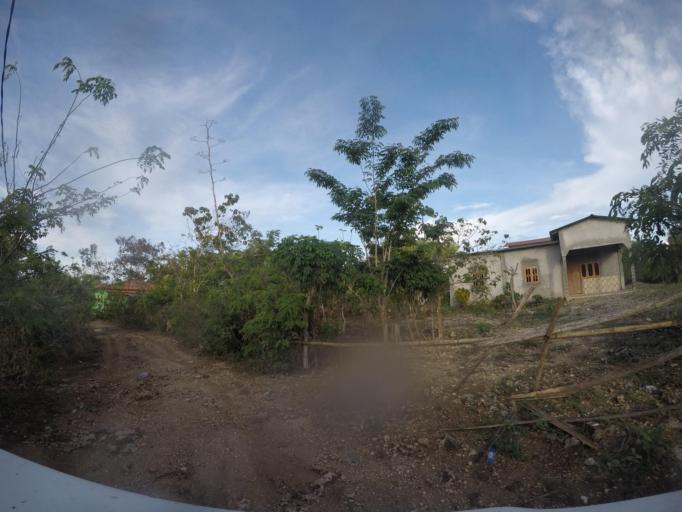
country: TL
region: Baucau
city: Baucau
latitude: -8.4874
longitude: 126.4505
